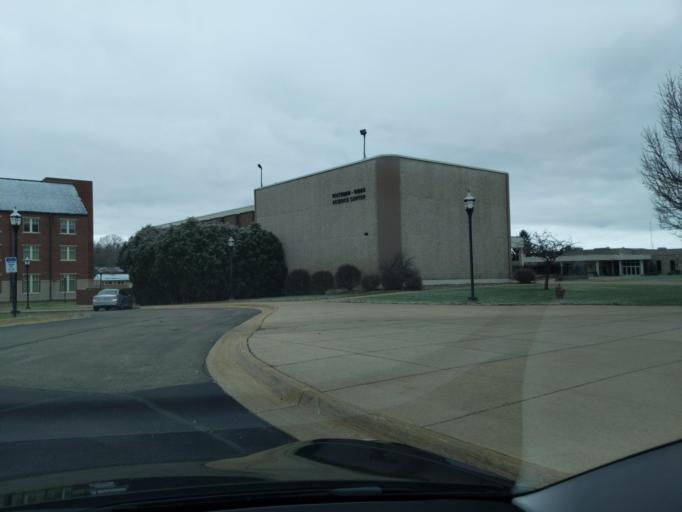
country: US
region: Michigan
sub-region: Jackson County
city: Spring Arbor
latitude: 42.2058
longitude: -84.5548
